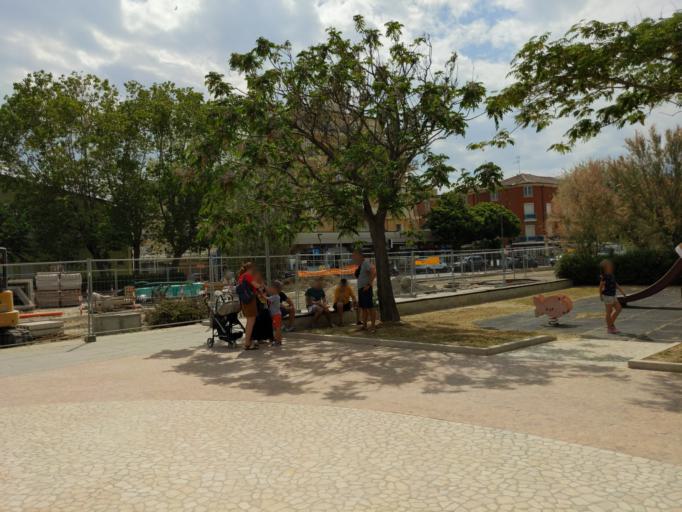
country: IT
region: Emilia-Romagna
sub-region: Provincia di Rimini
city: Rimini
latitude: 44.0784
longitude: 12.5536
